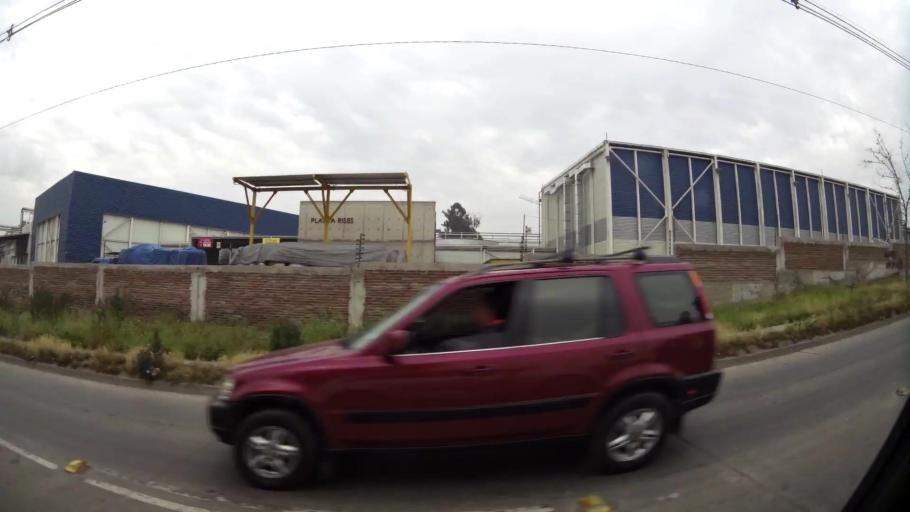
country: CL
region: Santiago Metropolitan
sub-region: Provincia de Santiago
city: Lo Prado
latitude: -33.4898
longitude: -70.7206
